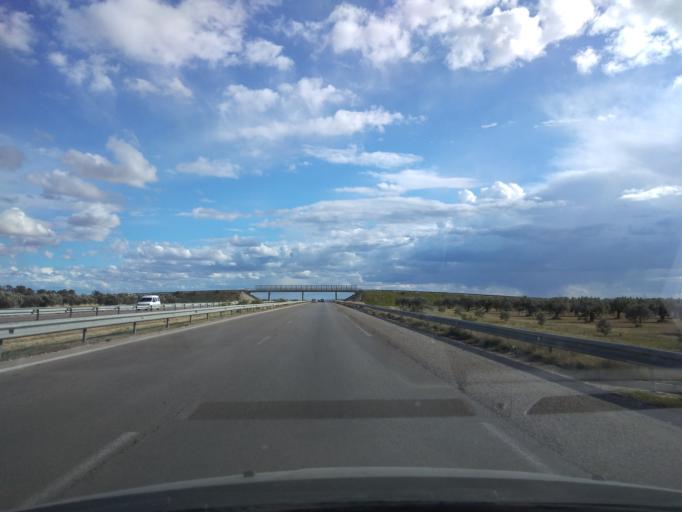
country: TN
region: Al Munastir
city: Manzil Kamil
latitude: 35.6208
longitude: 10.5943
